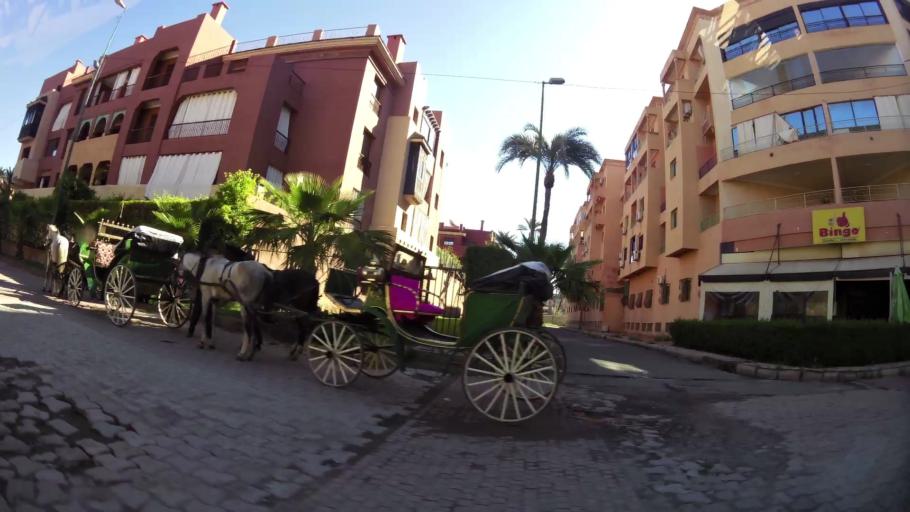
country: MA
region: Marrakech-Tensift-Al Haouz
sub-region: Marrakech
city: Marrakesh
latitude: 31.6467
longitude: -8.0175
